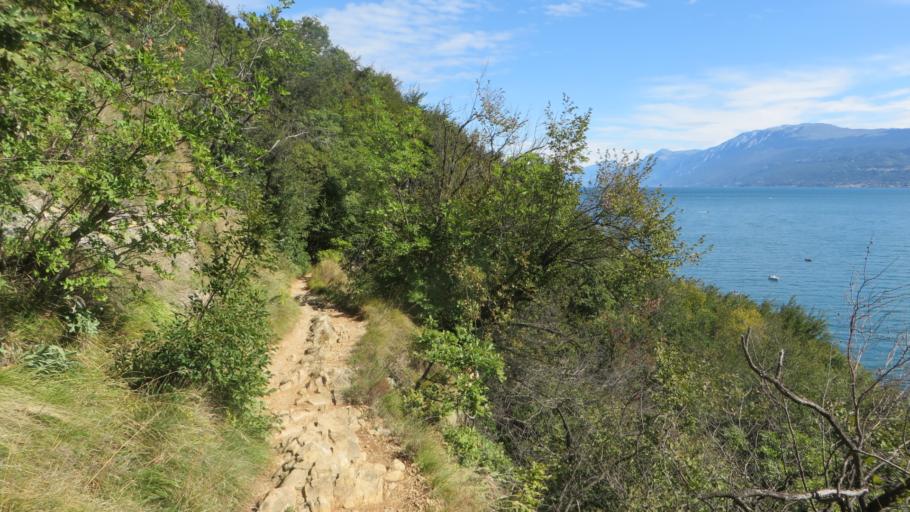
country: IT
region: Lombardy
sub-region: Provincia di Brescia
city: Solarolo
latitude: 45.5512
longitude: 10.5769
